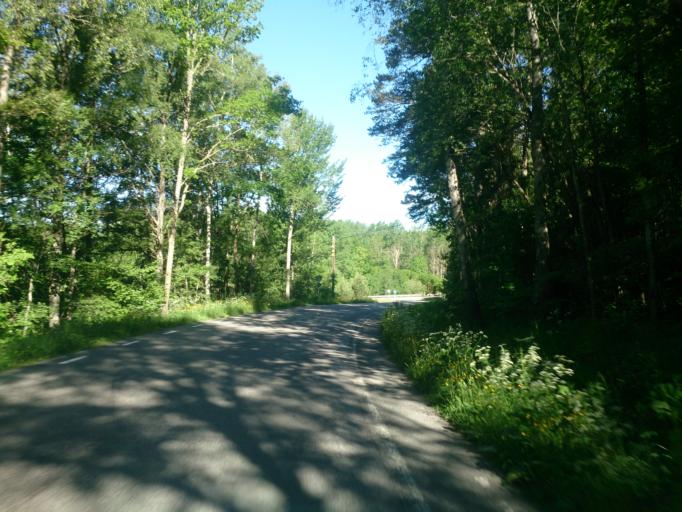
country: SE
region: OEstergoetland
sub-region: Atvidabergs Kommun
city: Atvidaberg
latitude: 58.1826
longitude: 16.0263
